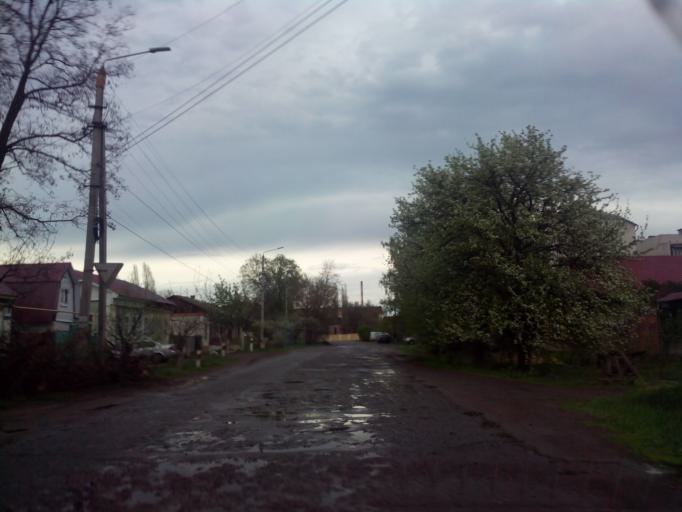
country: RU
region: Voronezj
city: Borisoglebsk
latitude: 51.3591
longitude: 42.0901
